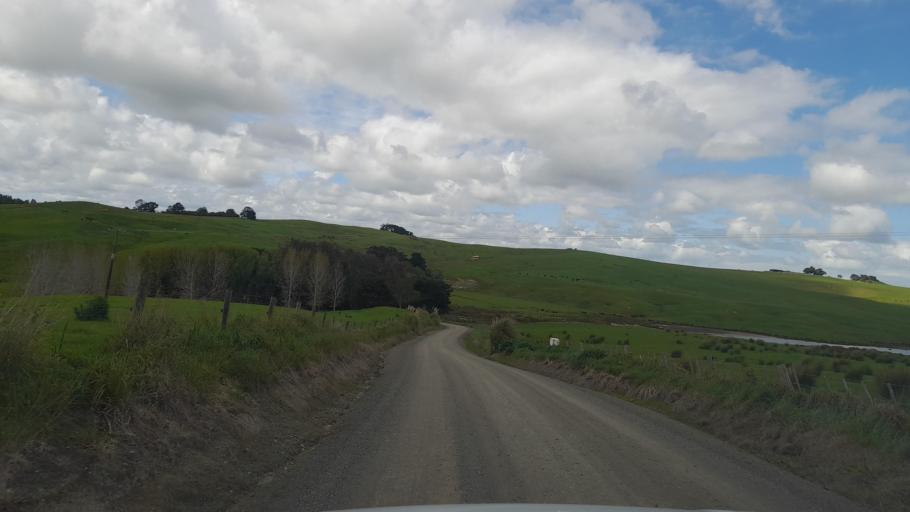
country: NZ
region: Auckland
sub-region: Auckland
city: Wellsford
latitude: -36.1915
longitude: 174.3262
